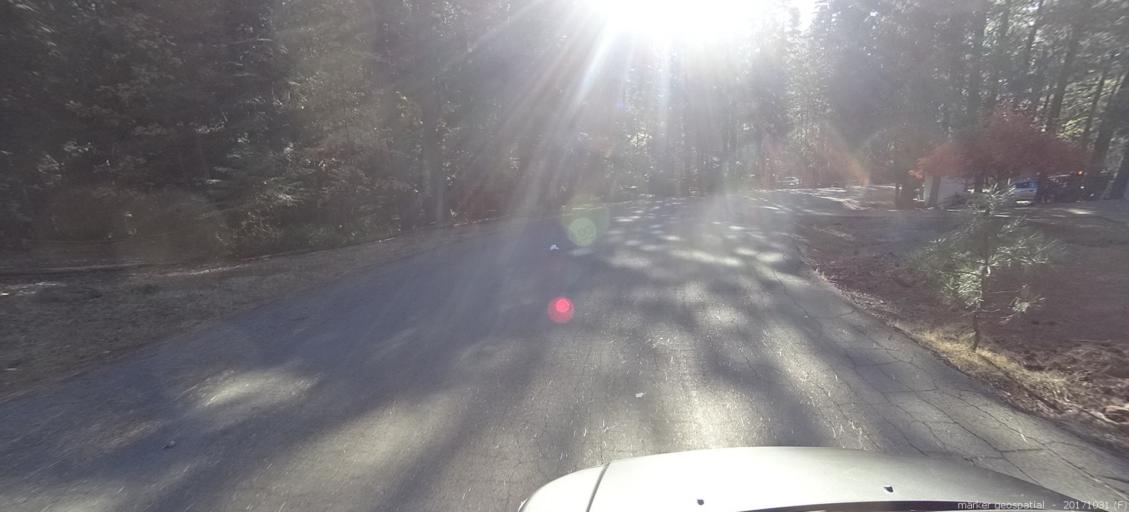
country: US
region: California
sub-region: Shasta County
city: Shingletown
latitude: 40.5011
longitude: -121.8992
